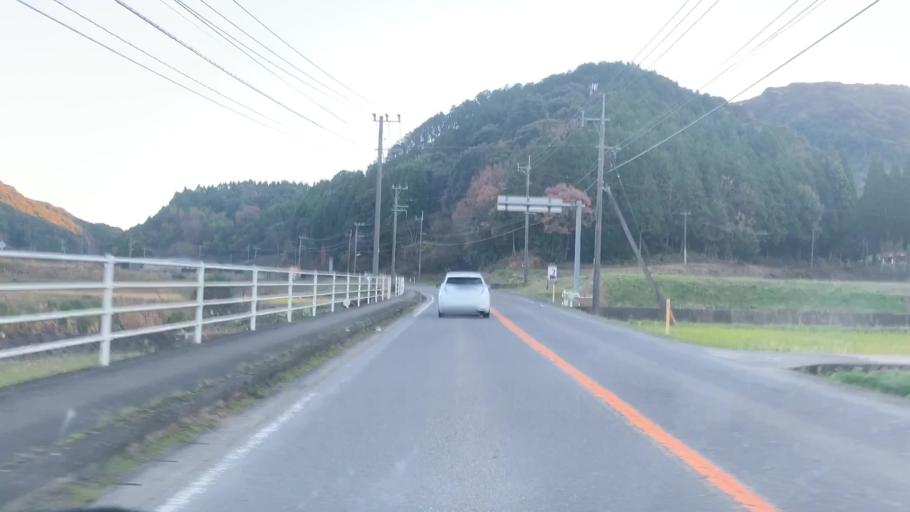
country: JP
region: Saga Prefecture
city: Takeocho-takeo
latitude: 33.2441
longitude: 130.0067
